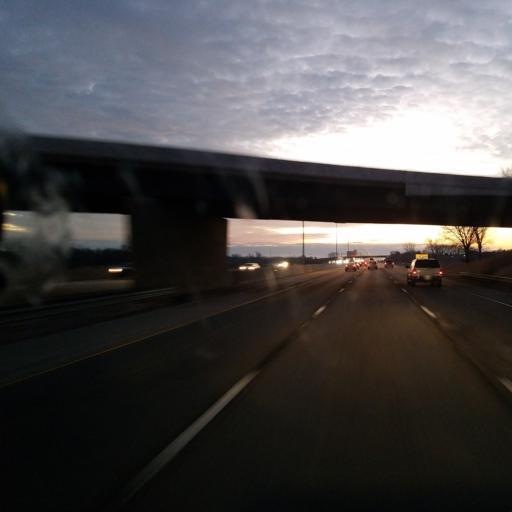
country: US
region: Illinois
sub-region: Tazewell County
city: Morton
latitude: 40.6295
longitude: -89.5082
